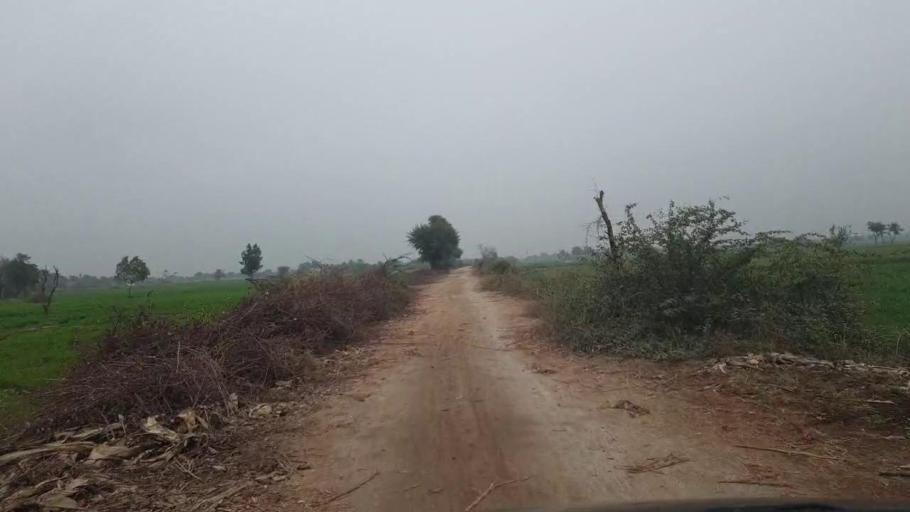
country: PK
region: Sindh
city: Tando Adam
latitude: 25.8462
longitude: 68.7038
